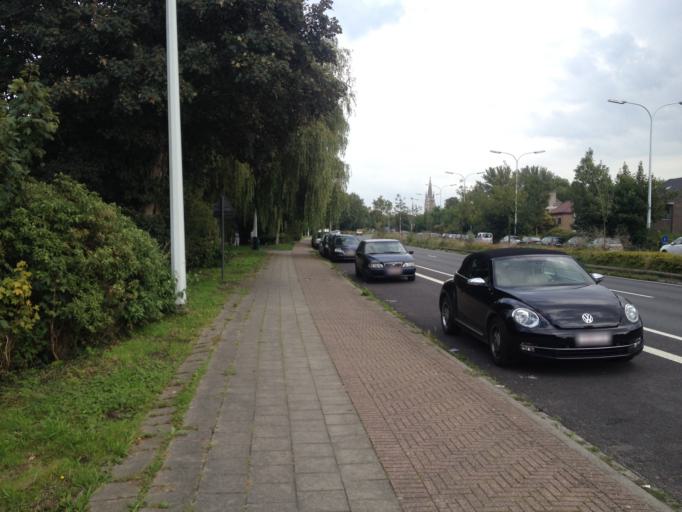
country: BE
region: Flanders
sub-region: Provincie West-Vlaanderen
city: Brugge
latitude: 51.2116
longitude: 3.2092
